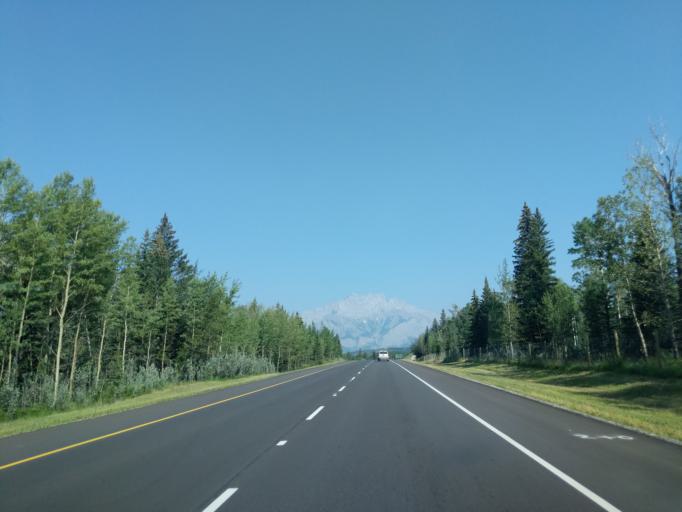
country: CA
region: Alberta
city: Canmore
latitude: 51.1471
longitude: -115.4240
